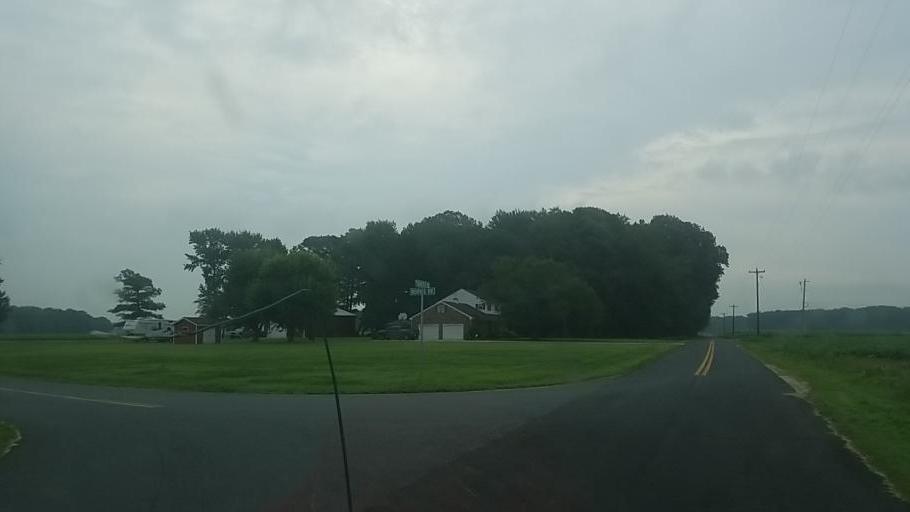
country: US
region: Delaware
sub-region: Sussex County
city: Selbyville
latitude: 38.4415
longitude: -75.2634
